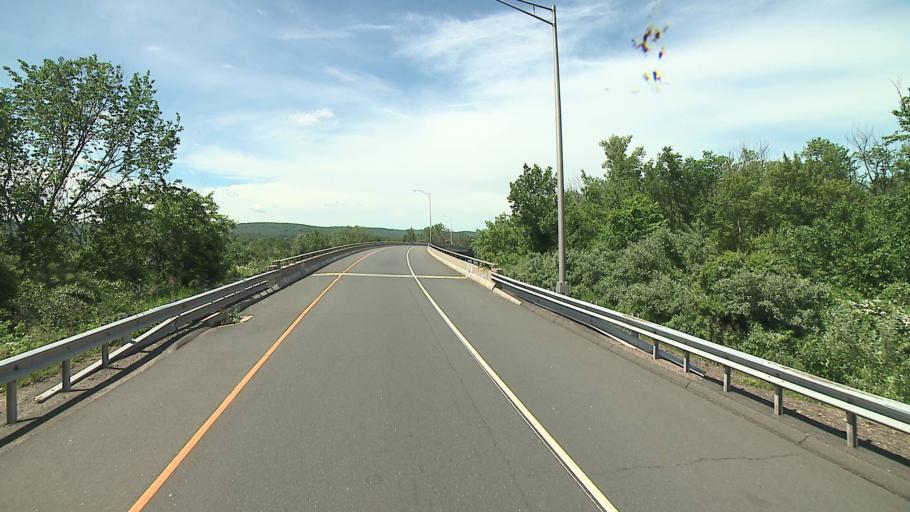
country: US
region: Connecticut
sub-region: New Haven County
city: Cheshire Village
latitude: 41.5616
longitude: -72.9111
